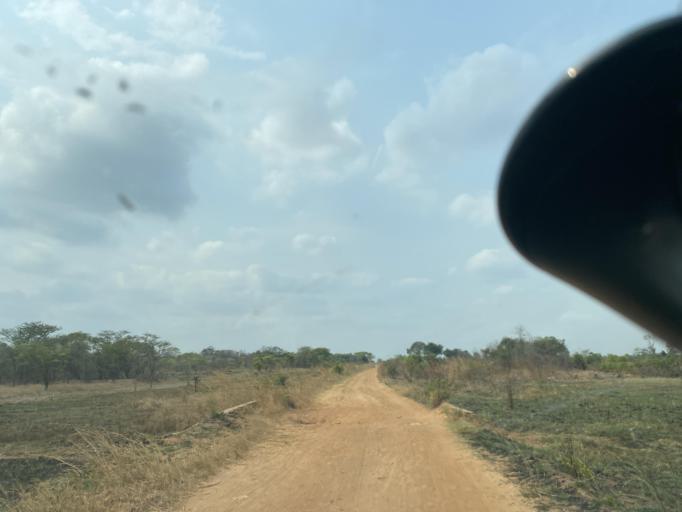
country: ZM
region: Lusaka
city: Lusaka
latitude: -15.1416
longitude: 28.3669
